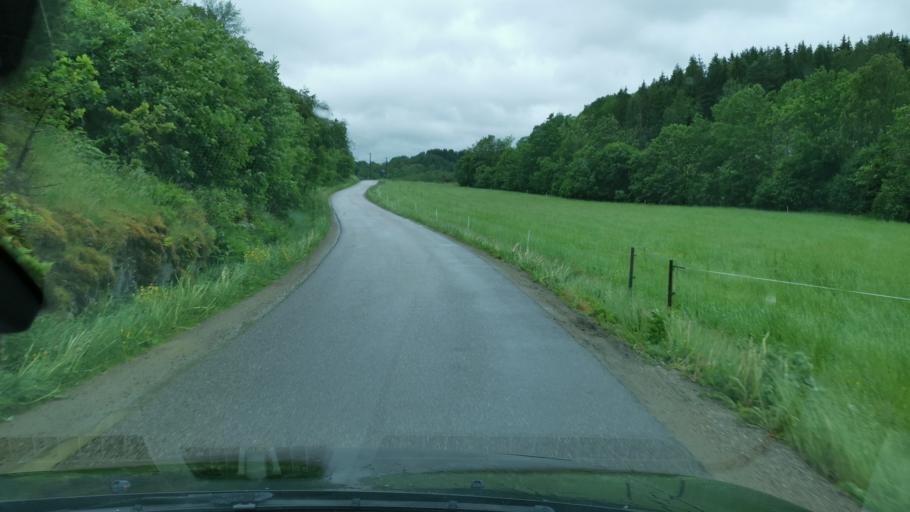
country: SE
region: Vaestra Goetaland
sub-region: Orust
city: Henan
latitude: 58.3281
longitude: 11.6991
